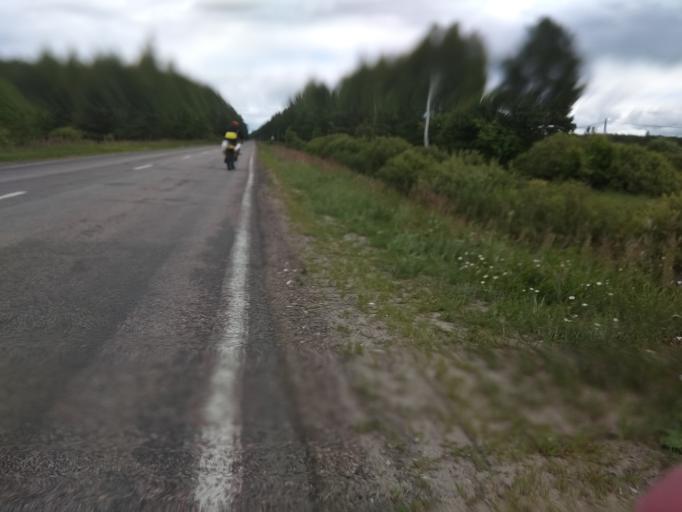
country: RU
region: Moskovskaya
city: Misheronskiy
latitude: 55.6088
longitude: 39.7140
